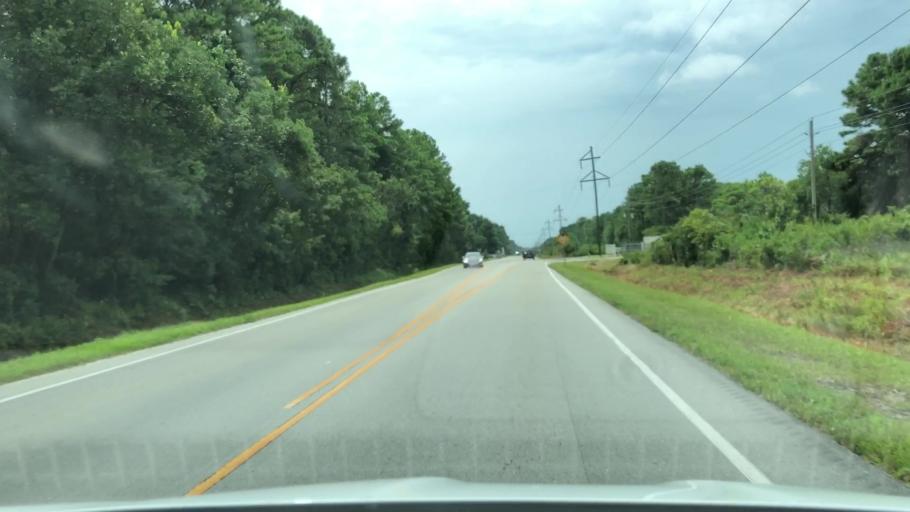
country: US
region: North Carolina
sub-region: Carteret County
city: Newport
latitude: 34.7561
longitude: -76.8743
